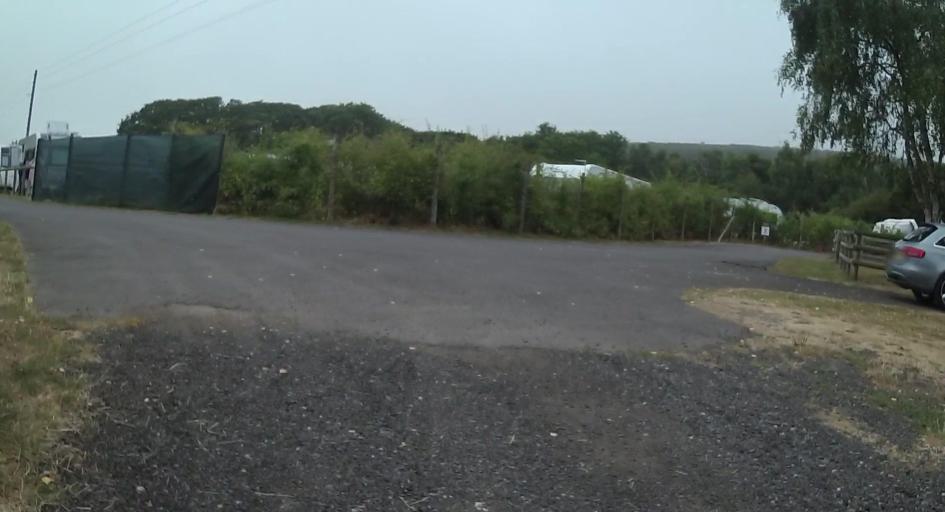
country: GB
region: England
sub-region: Dorset
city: Wareham
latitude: 50.6458
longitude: -2.0755
